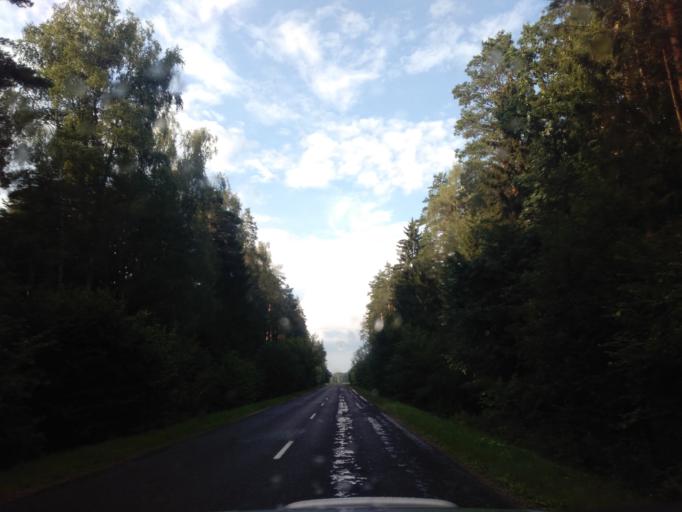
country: BY
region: Minsk
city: Kapyl'
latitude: 53.2748
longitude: 27.0770
